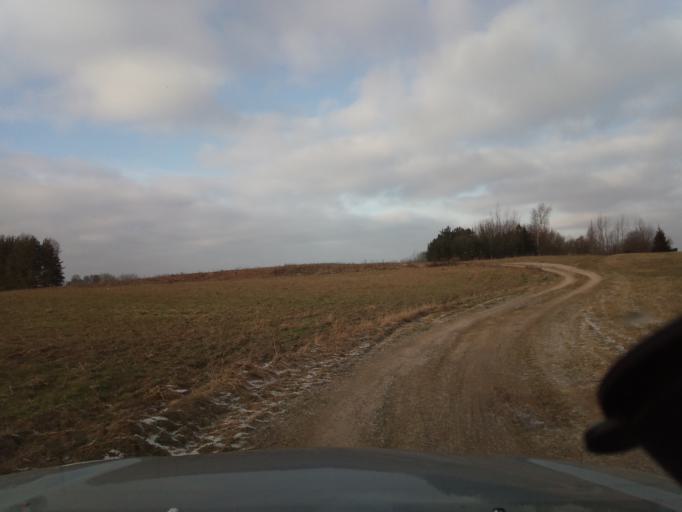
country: LT
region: Alytaus apskritis
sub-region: Alytaus rajonas
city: Daugai
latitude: 54.3783
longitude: 24.4166
